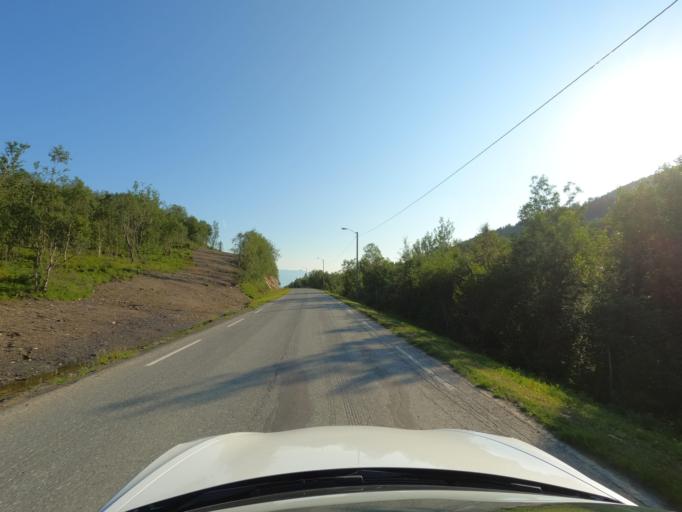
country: NO
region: Nordland
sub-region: Narvik
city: Bjerkvik
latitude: 68.5421
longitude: 17.4932
